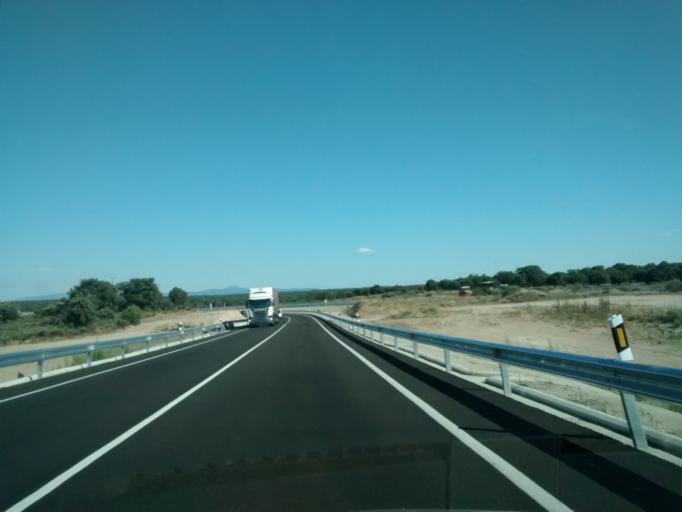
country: ES
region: Castille and Leon
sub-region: Provincia de Salamanca
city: Fuentes de Onoro
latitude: 40.5902
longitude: -6.7806
